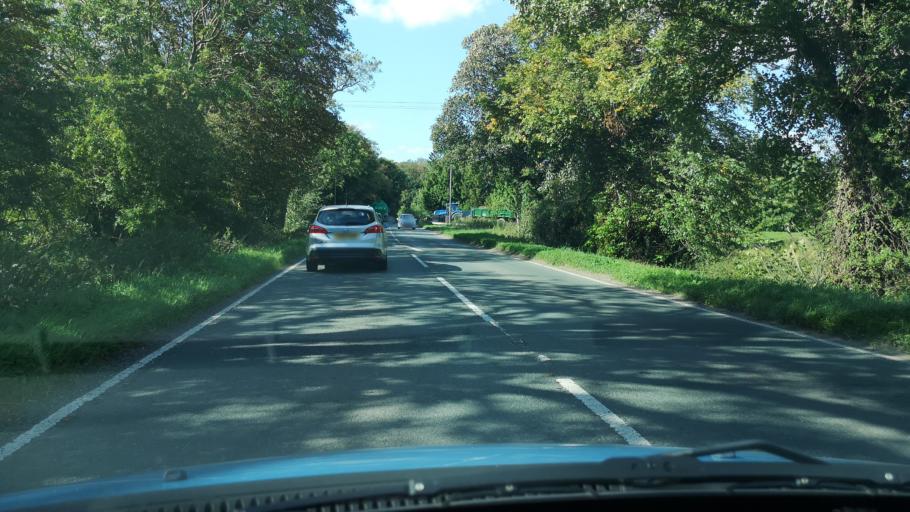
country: GB
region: England
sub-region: North Lincolnshire
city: Belton
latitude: 53.5778
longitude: -0.8196
